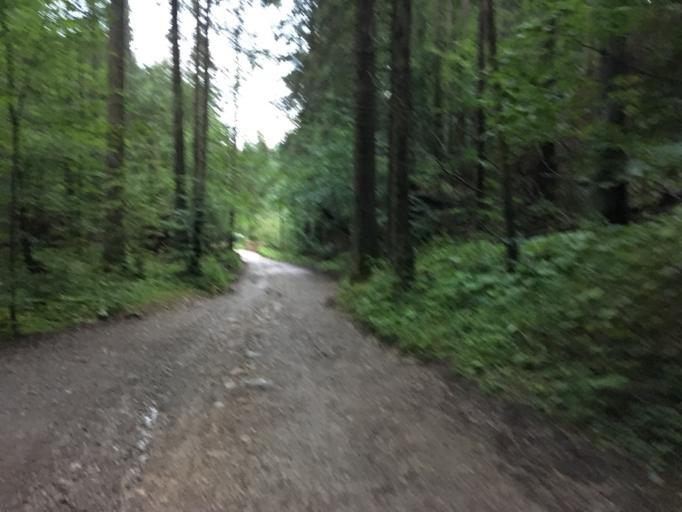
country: PL
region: Lesser Poland Voivodeship
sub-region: Powiat tatrzanski
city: Zakopane
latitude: 49.2773
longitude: 19.9367
